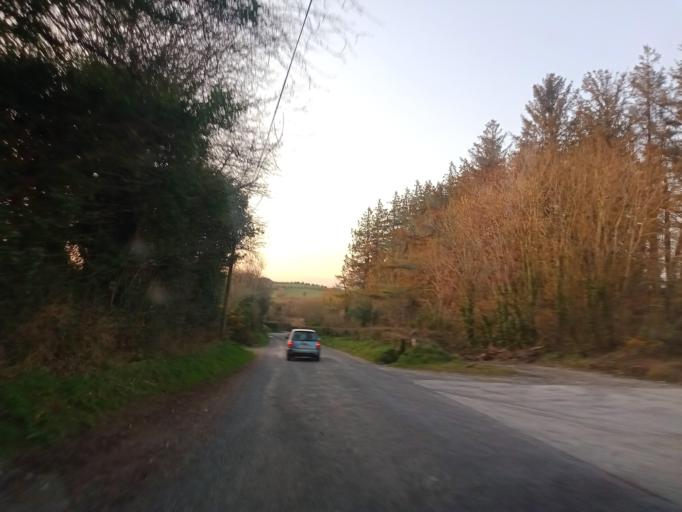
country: IE
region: Leinster
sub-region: Kilkenny
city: Castlecomer
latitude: 52.8599
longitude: -7.2677
